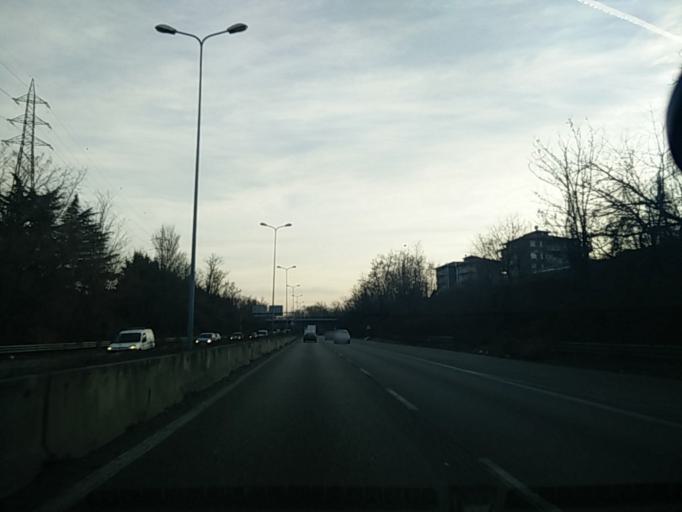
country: IT
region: Lombardy
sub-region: Provincia di Monza e Brianza
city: Bovisio-Masciago
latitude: 45.6121
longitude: 9.1654
